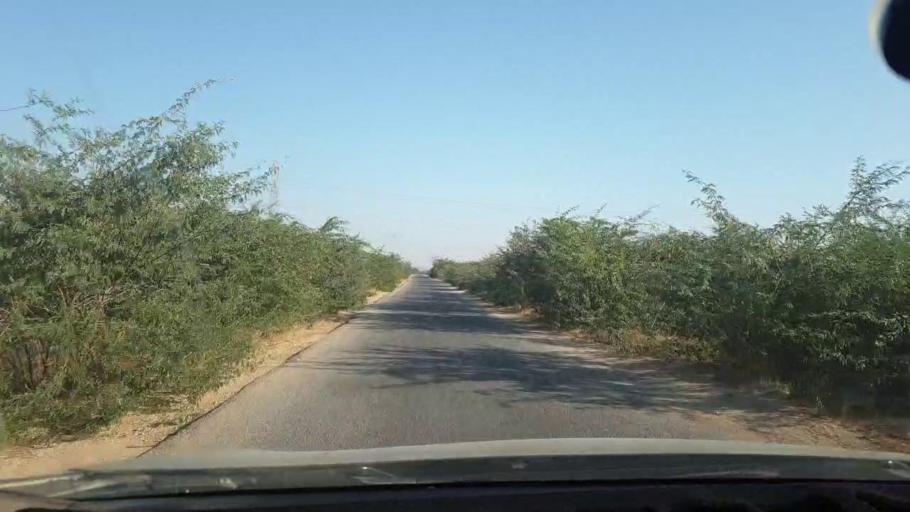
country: PK
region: Sindh
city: Malir Cantonment
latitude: 25.1588
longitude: 67.1934
